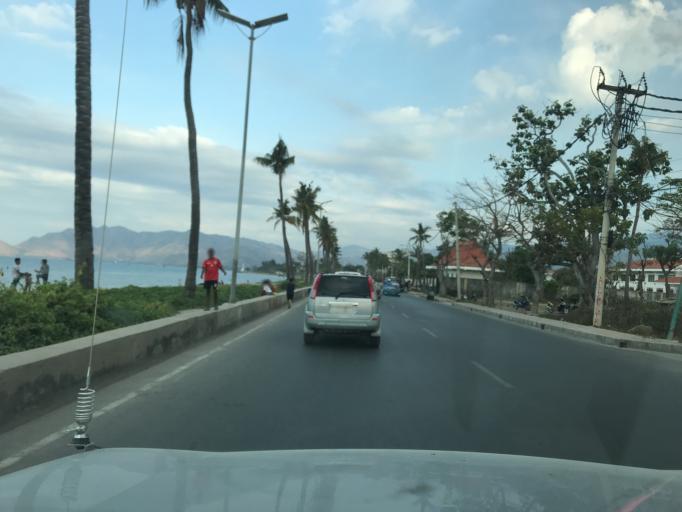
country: TL
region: Dili
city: Dili
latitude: -8.5470
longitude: 125.5550
